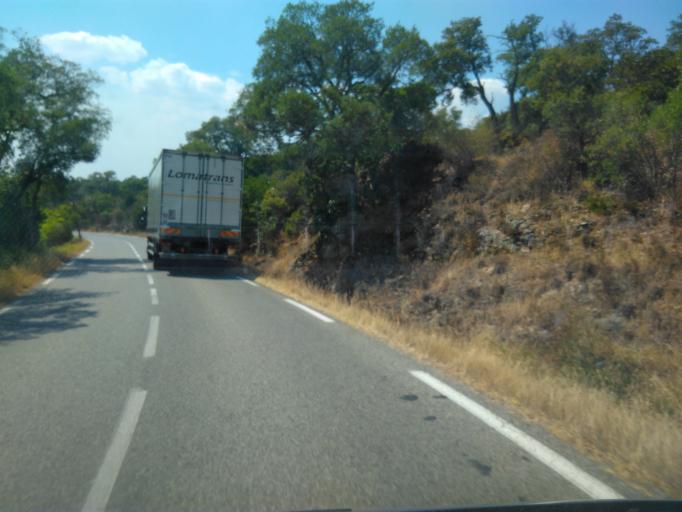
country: FR
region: Provence-Alpes-Cote d'Azur
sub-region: Departement du Var
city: La Garde-Freinet
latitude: 43.3333
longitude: 6.4327
